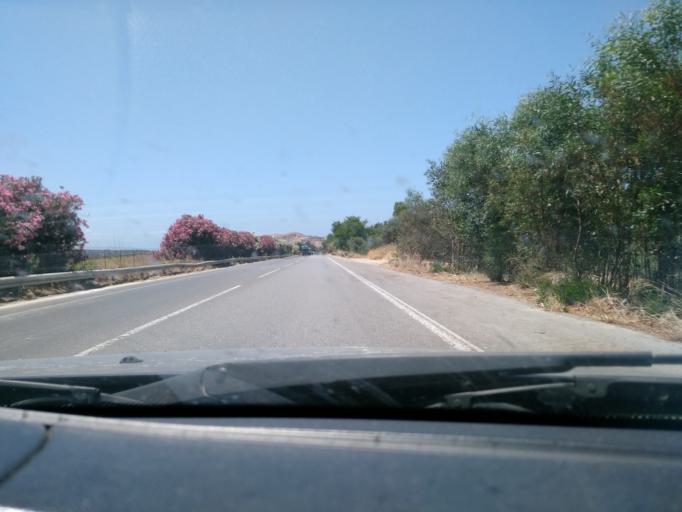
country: GR
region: Crete
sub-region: Nomos Rethymnis
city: Panormos
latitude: 35.4146
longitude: 24.7049
